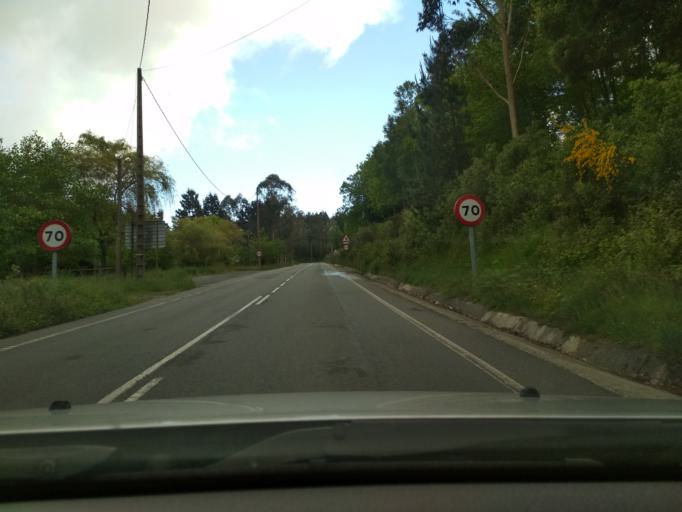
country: ES
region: Galicia
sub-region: Provincia da Coruna
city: Carballo
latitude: 43.0992
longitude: -8.6837
